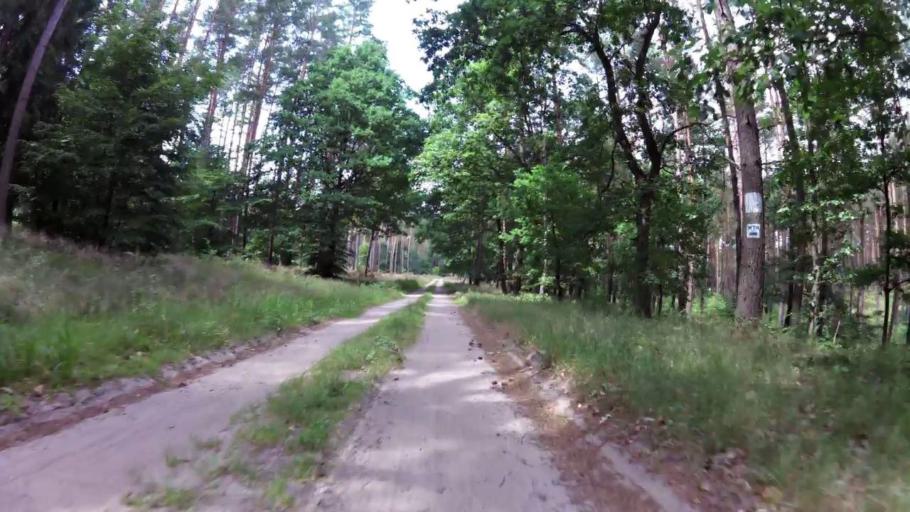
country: PL
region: West Pomeranian Voivodeship
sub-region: Powiat lobeski
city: Lobez
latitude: 53.5570
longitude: 15.6705
